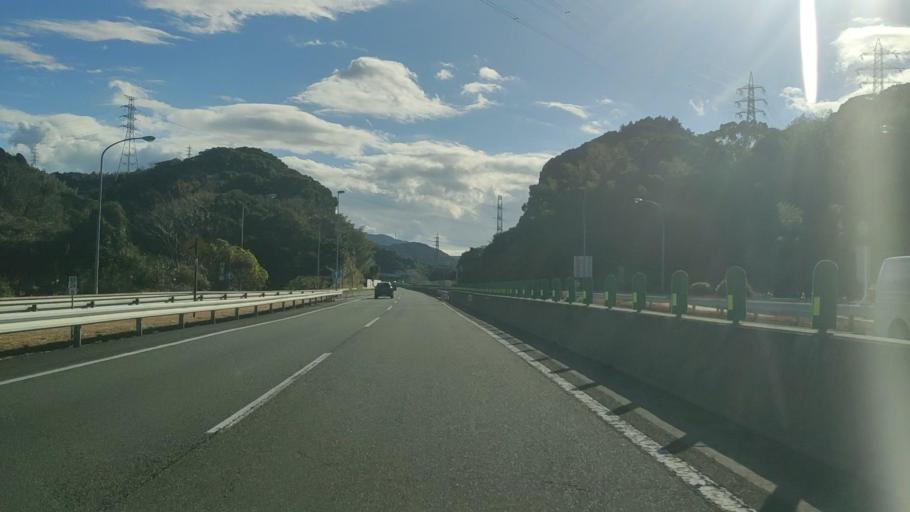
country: JP
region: Fukuoka
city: Kitakyushu
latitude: 33.8401
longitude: 130.7653
